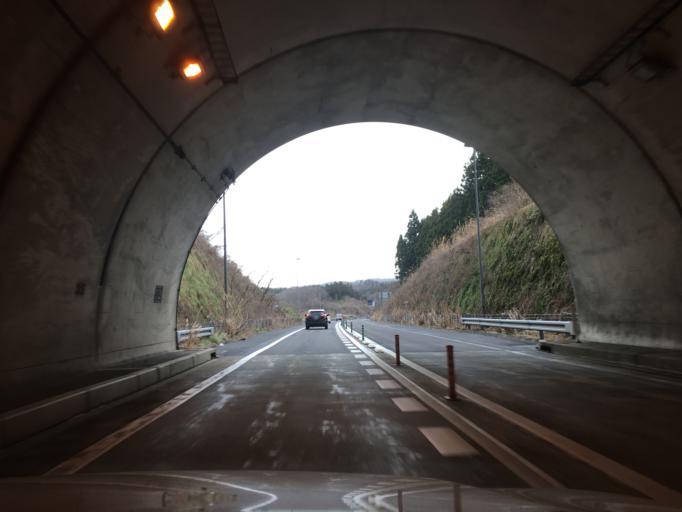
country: JP
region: Yamagata
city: Yuza
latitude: 39.3175
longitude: 139.9912
